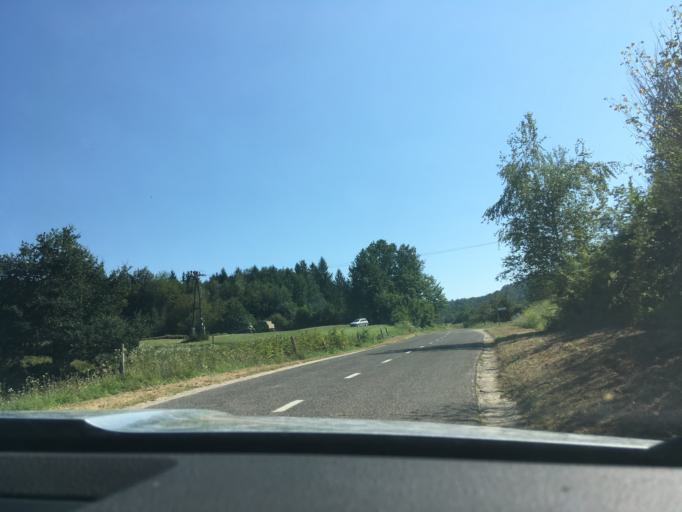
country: SI
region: Metlika
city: Metlika
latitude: 45.5412
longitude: 15.2945
